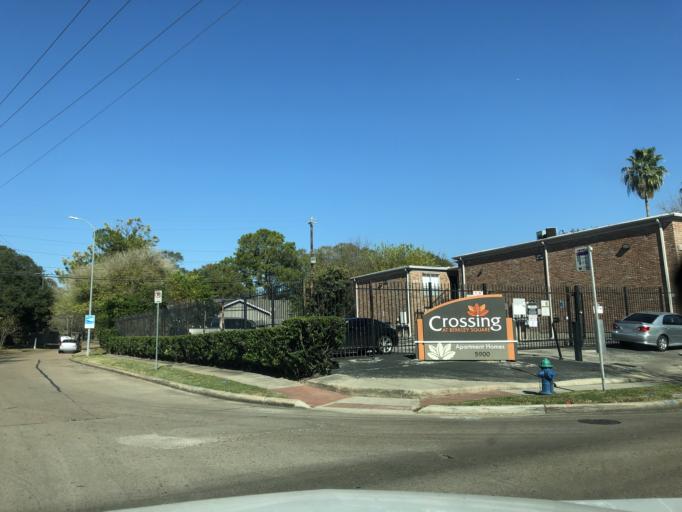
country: US
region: Texas
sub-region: Harris County
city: Bellaire
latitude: 29.6793
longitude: -95.4975
